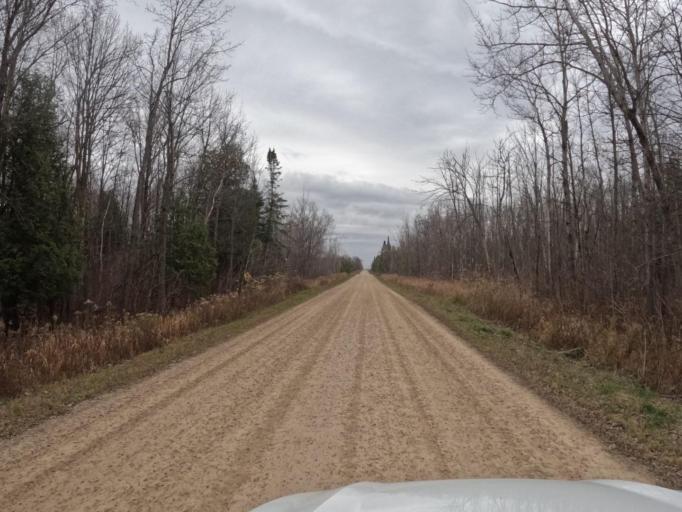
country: CA
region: Ontario
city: Shelburne
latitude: 44.0293
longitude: -80.3939
